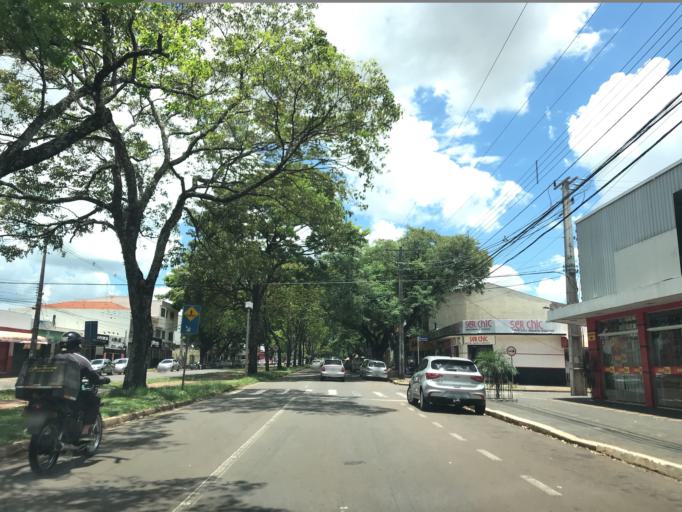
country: BR
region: Parana
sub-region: Maringa
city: Maringa
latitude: -23.3970
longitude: -51.9188
